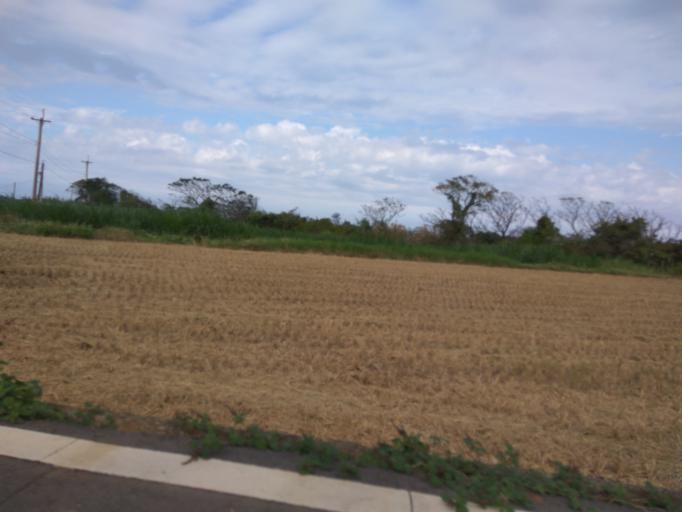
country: TW
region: Taiwan
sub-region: Hsinchu
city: Zhubei
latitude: 24.9486
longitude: 121.0040
